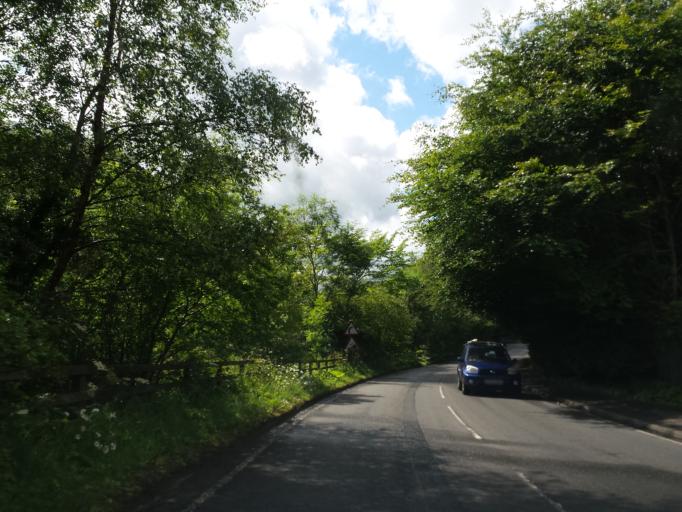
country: GB
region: Scotland
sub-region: Midlothian
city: Loanhead
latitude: 55.8519
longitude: -3.1678
